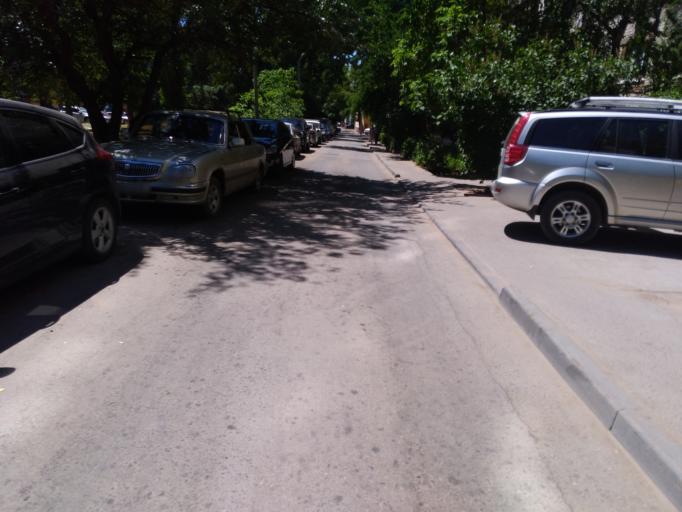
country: RU
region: Volgograd
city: Volgograd
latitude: 48.7145
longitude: 44.5001
